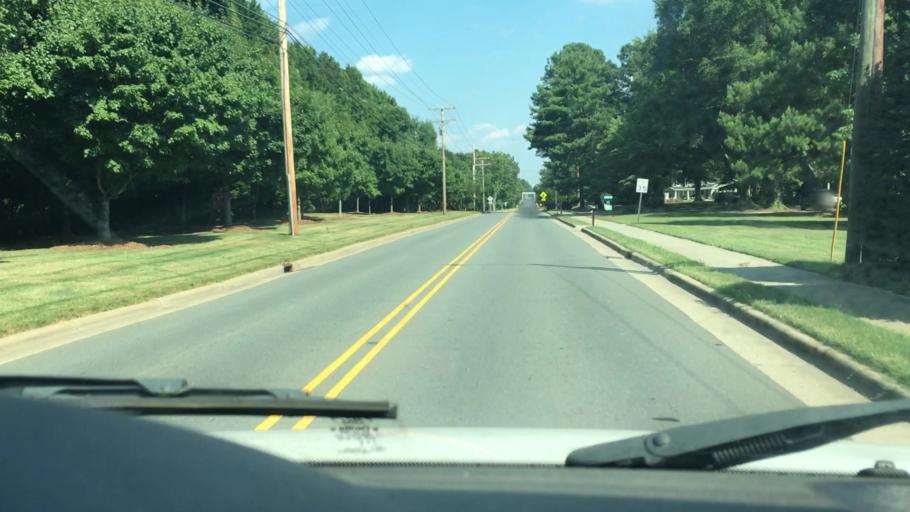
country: US
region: North Carolina
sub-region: Gaston County
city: Davidson
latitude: 35.4907
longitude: -80.8307
